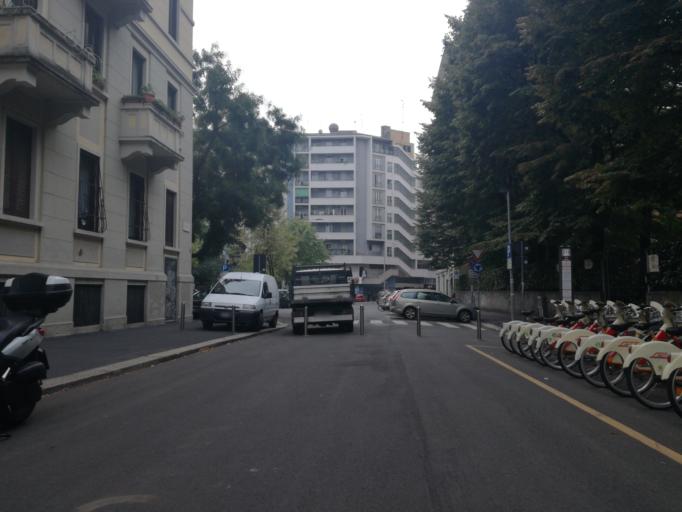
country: IT
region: Lombardy
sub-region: Citta metropolitana di Milano
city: Milano
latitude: 45.4707
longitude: 9.2259
